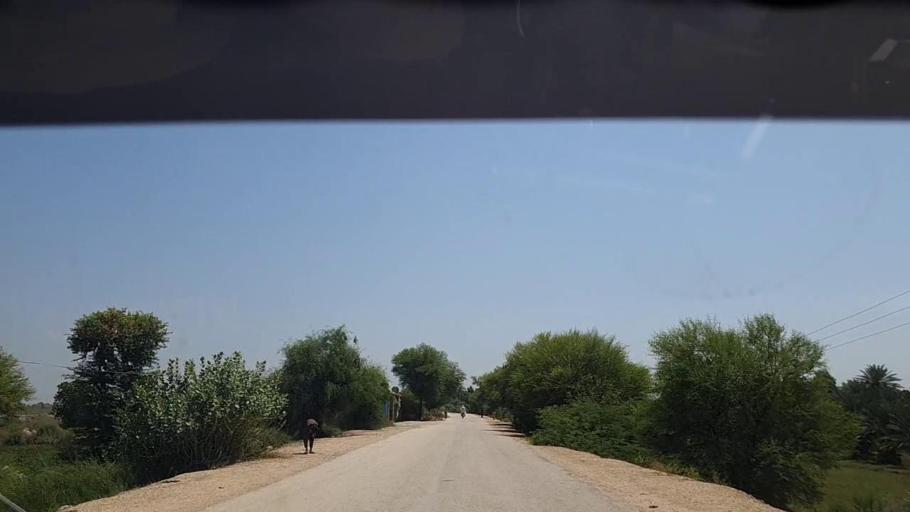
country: PK
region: Sindh
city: Ghauspur
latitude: 28.1634
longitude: 69.1386
